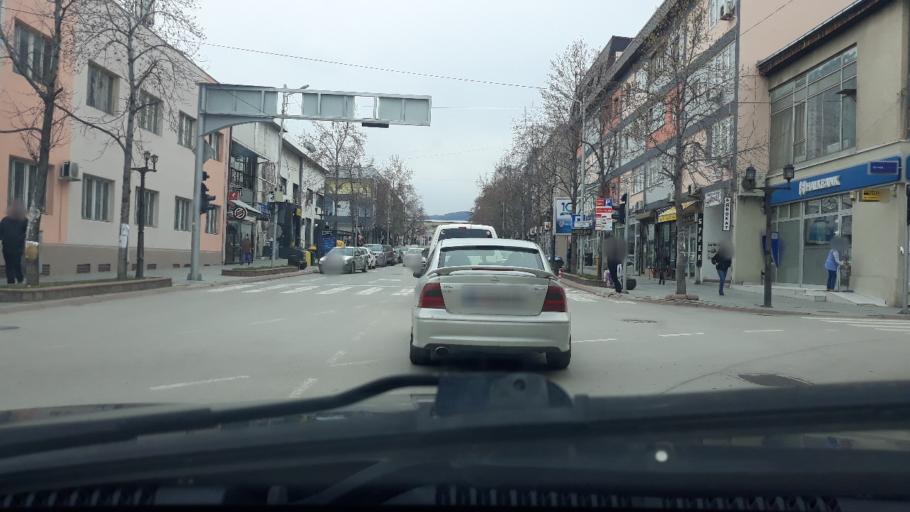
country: MK
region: Kavadarci
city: Kavadarci
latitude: 41.4351
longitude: 22.0115
